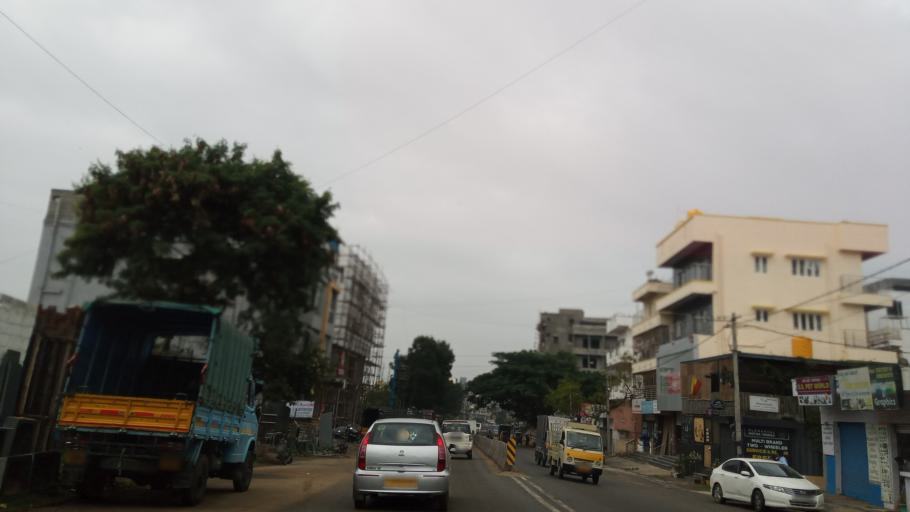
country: IN
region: Karnataka
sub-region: Bangalore Urban
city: Bangalore
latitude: 12.9036
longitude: 77.5245
